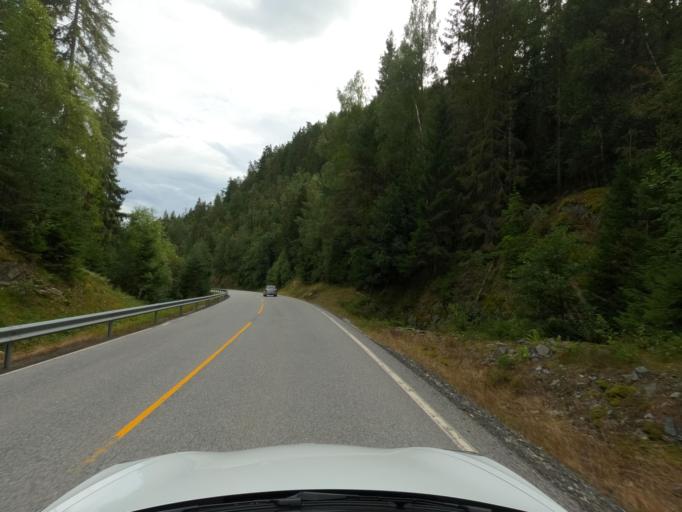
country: NO
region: Telemark
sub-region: Hjartdal
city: Sauland
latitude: 59.8202
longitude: 8.9821
